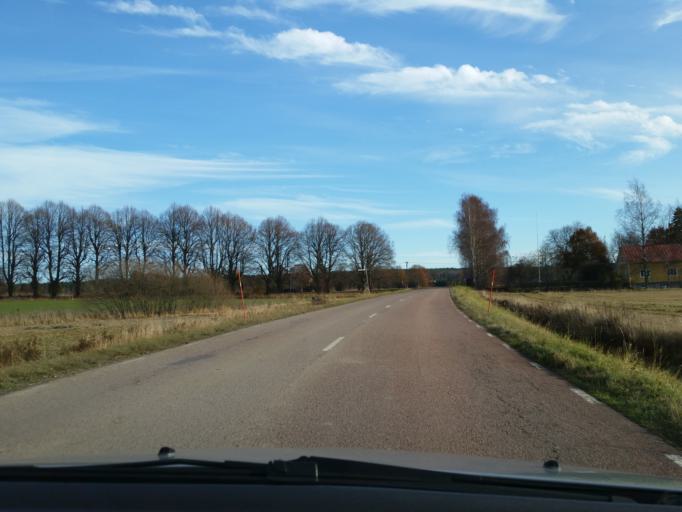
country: AX
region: Alands landsbygd
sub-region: Saltvik
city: Saltvik
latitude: 60.3217
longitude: 20.0154
